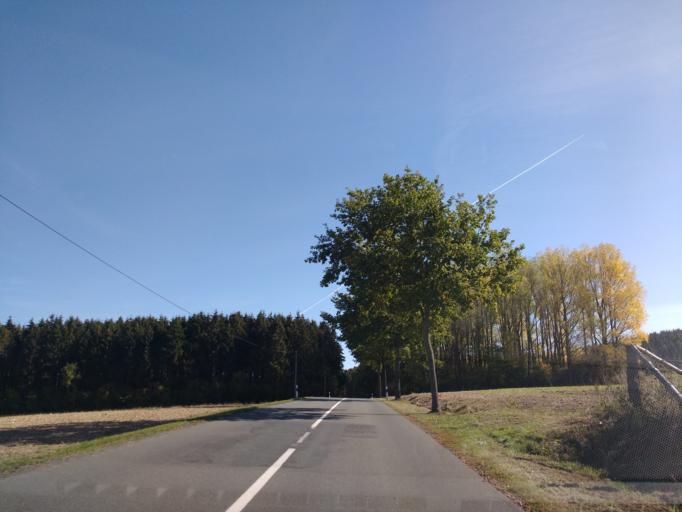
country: DE
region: North Rhine-Westphalia
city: Lichtenau
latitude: 51.6190
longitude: 8.9275
